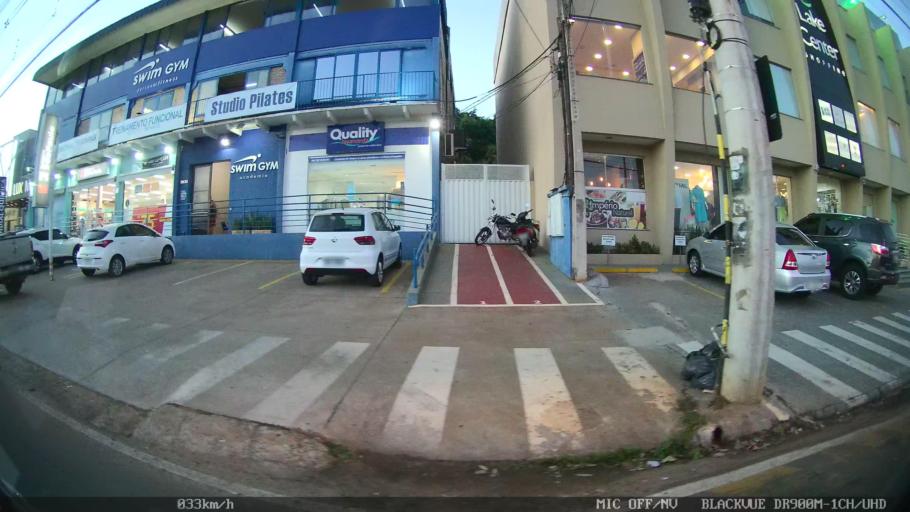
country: BR
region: Sao Paulo
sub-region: Sao Jose Do Rio Preto
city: Sao Jose do Rio Preto
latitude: -20.8095
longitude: -49.3533
